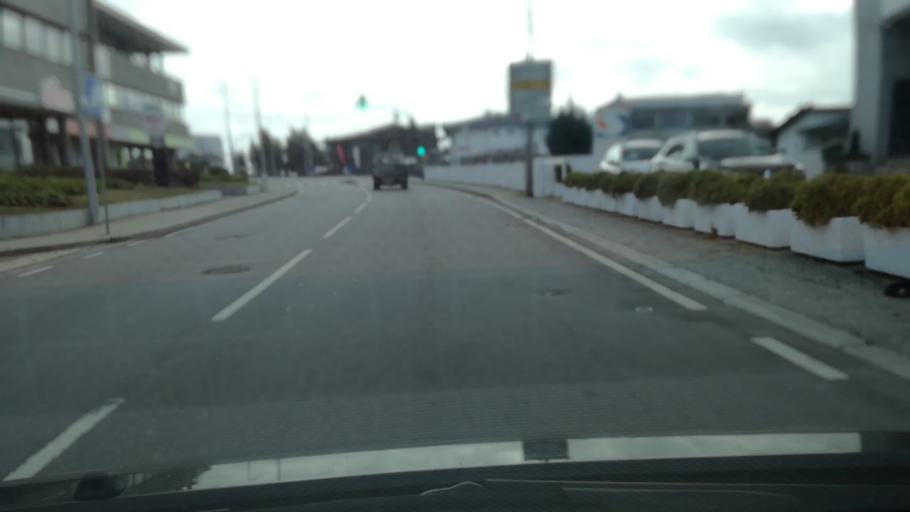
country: PT
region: Porto
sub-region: Maia
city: Gemunde
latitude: 41.2579
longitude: -8.6450
